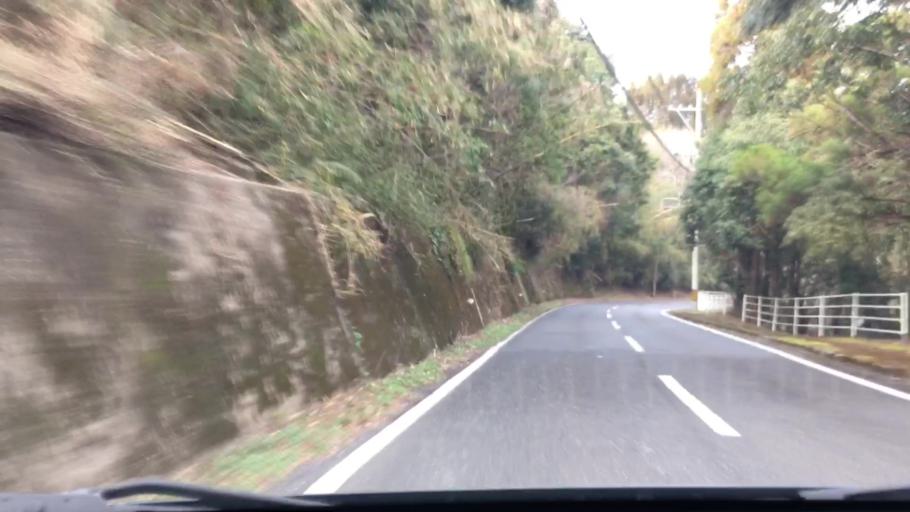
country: JP
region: Miyazaki
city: Kushima
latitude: 31.5422
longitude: 131.2419
